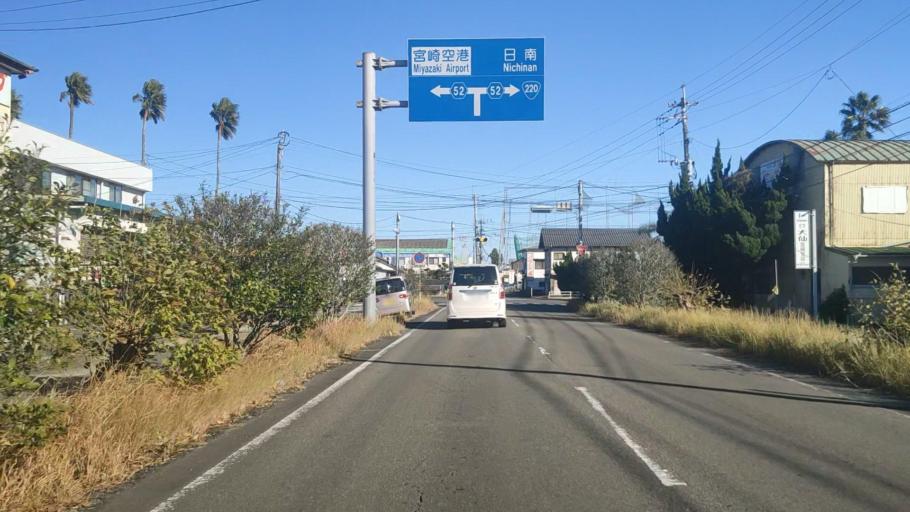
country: JP
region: Miyazaki
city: Miyazaki-shi
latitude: 31.8698
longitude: 131.4359
